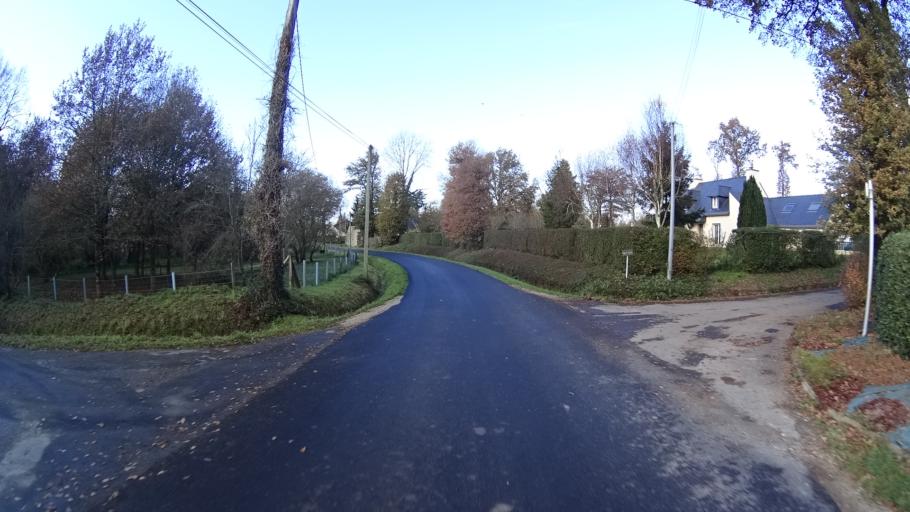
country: FR
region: Brittany
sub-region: Departement du Morbihan
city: La Gacilly
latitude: 47.7886
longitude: -2.1441
